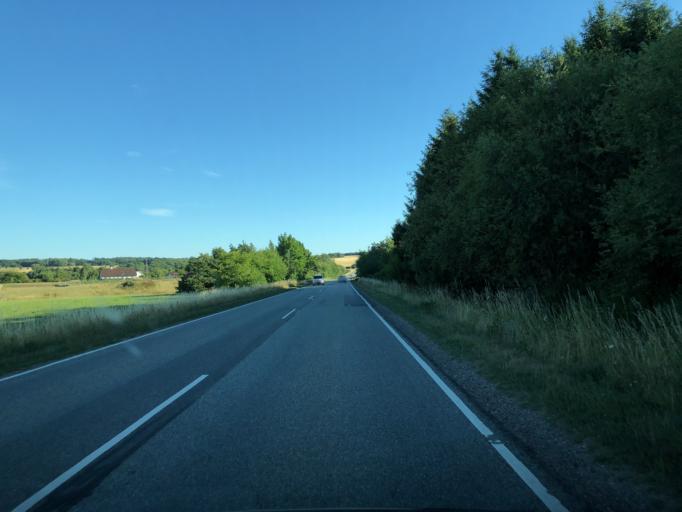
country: DK
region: Central Jutland
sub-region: Arhus Kommune
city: Framlev
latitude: 56.1321
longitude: 9.9970
